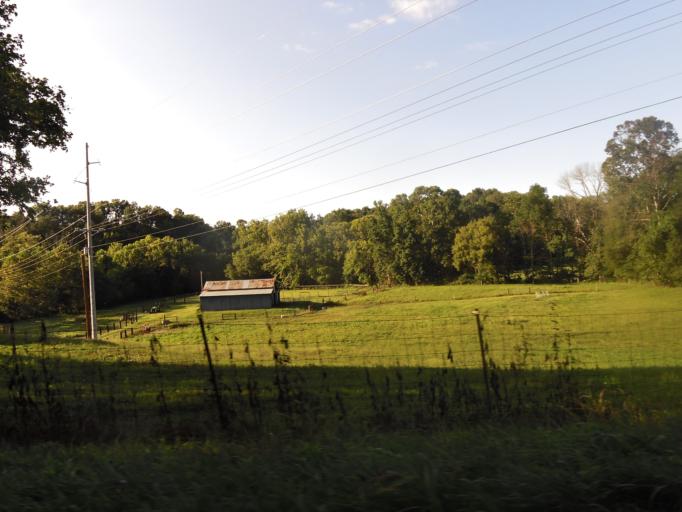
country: US
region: Tennessee
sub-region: Union County
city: Condon
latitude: 36.1913
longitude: -83.8228
